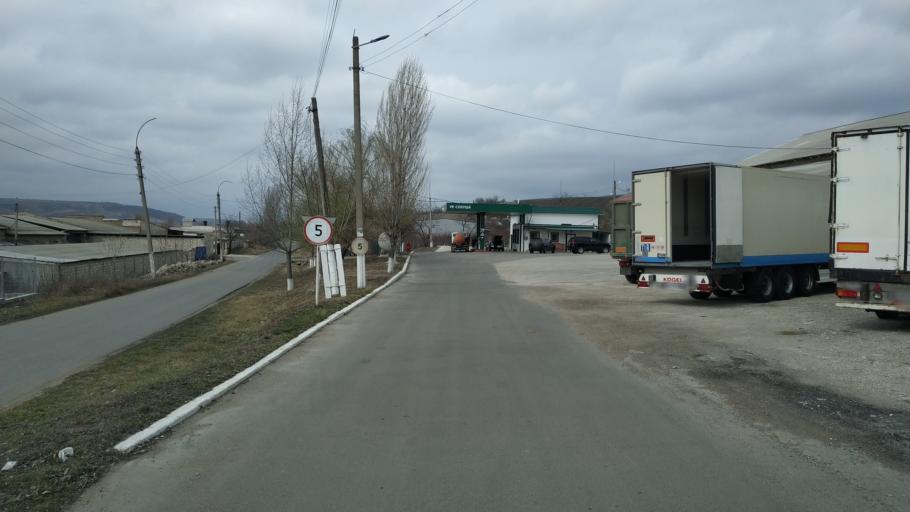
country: MD
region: Laloveni
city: Ialoveni
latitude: 46.8795
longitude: 28.7665
